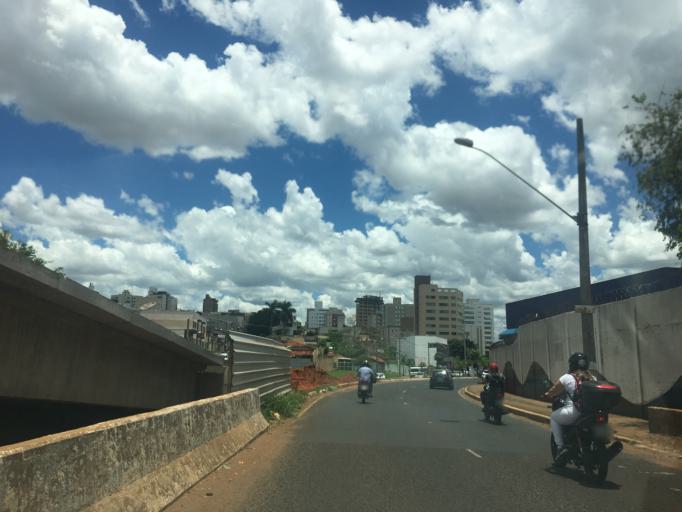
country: BR
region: Minas Gerais
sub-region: Uberlandia
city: Uberlandia
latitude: -18.9298
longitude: -48.2929
